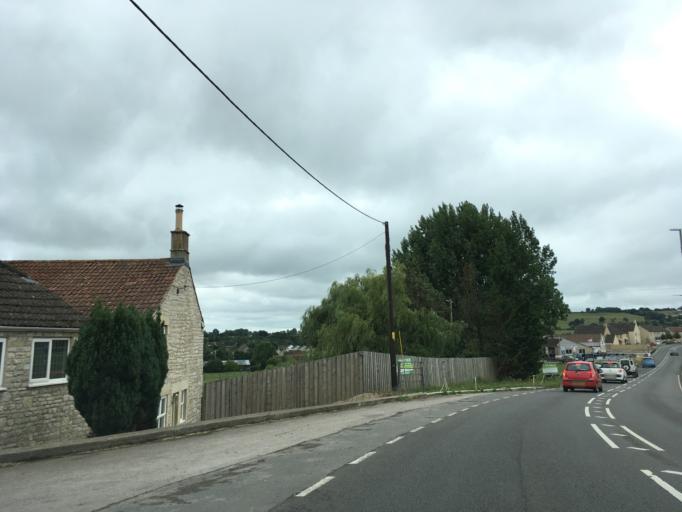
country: GB
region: England
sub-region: Bath and North East Somerset
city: Timsbury
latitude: 51.3481
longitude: -2.4839
